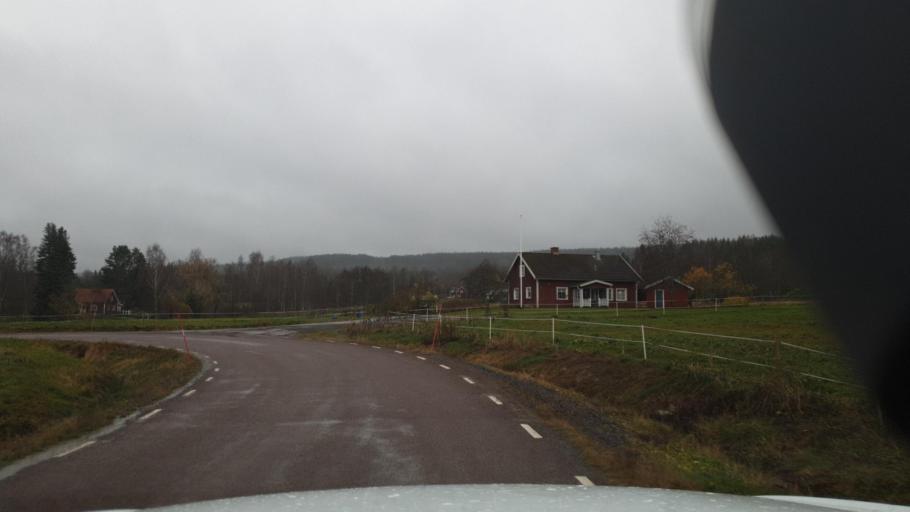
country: SE
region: Vaermland
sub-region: Sunne Kommun
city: Sunne
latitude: 59.7421
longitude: 13.0593
